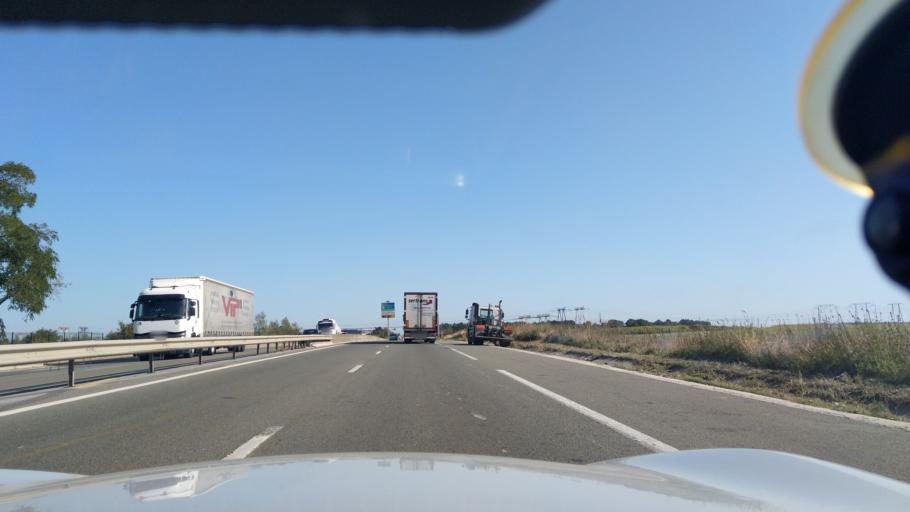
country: FR
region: Ile-de-France
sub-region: Departement du Val-d'Oise
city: Le Thillay
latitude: 48.9899
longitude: 2.4753
